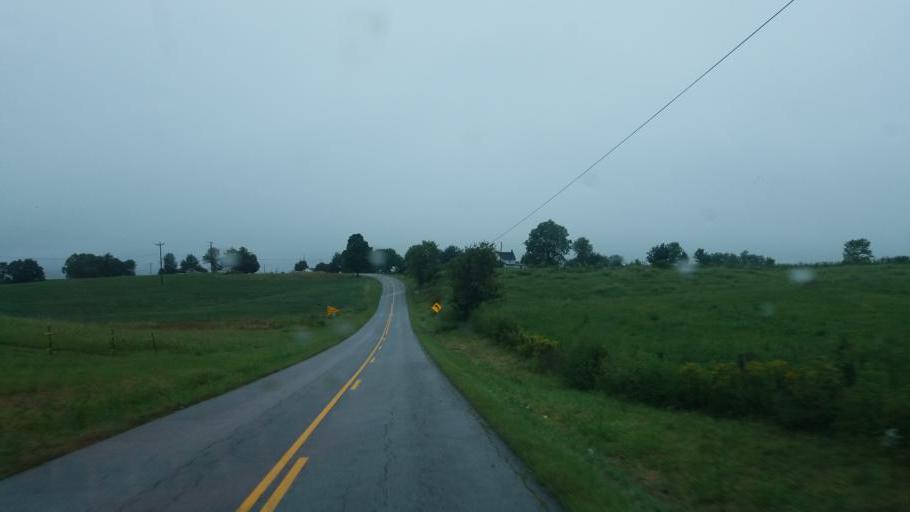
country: US
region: Kentucky
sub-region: Fleming County
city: Flemingsburg
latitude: 38.4145
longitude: -83.6698
